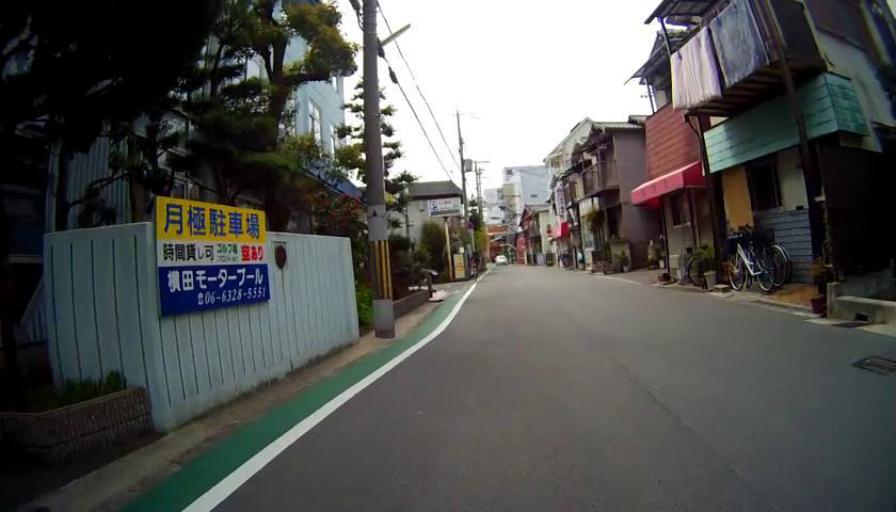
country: JP
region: Osaka
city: Suita
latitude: 34.7537
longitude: 135.5310
